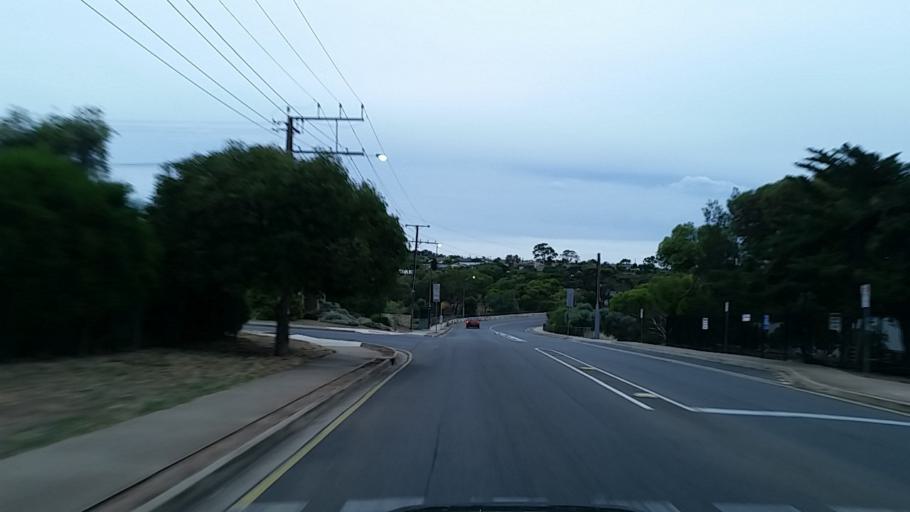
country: AU
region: South Australia
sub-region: Adelaide
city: Port Noarlunga
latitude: -35.1247
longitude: 138.4798
